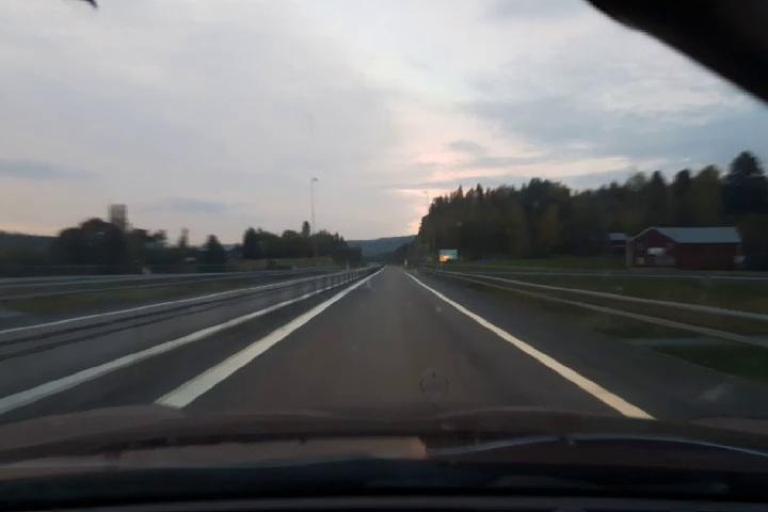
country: SE
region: Vaesternorrland
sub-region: Kramfors Kommun
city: Nordingra
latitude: 62.9298
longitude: 18.0969
